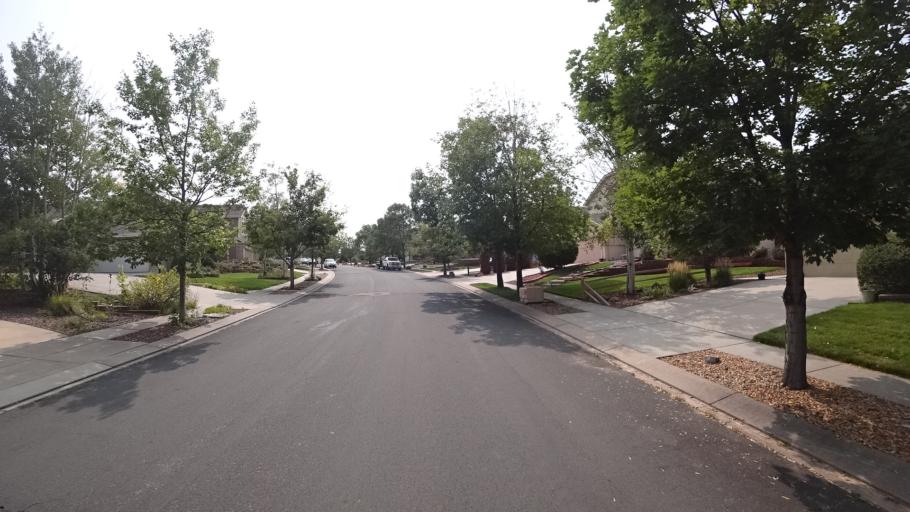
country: US
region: Colorado
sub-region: El Paso County
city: Cimarron Hills
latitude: 38.9249
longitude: -104.7471
